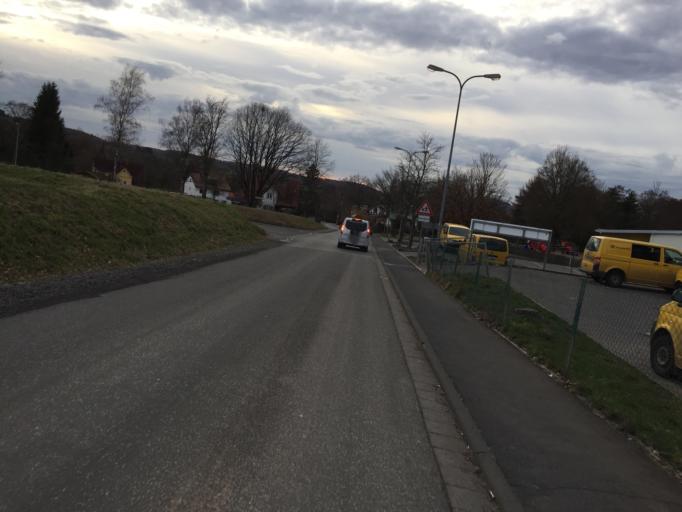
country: DE
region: Hesse
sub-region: Regierungsbezirk Giessen
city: Rabenau
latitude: 50.6747
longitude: 8.8700
